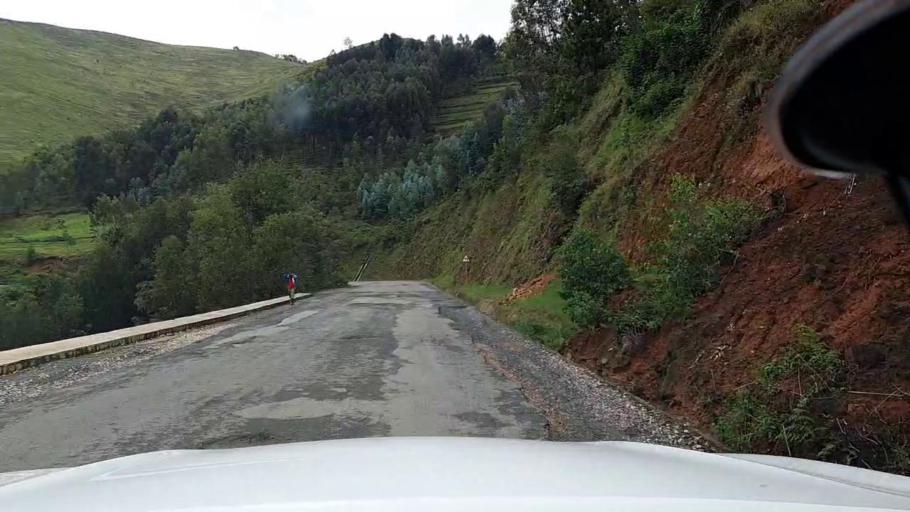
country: RW
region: Southern Province
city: Gitarama
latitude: -2.0619
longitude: 29.5621
